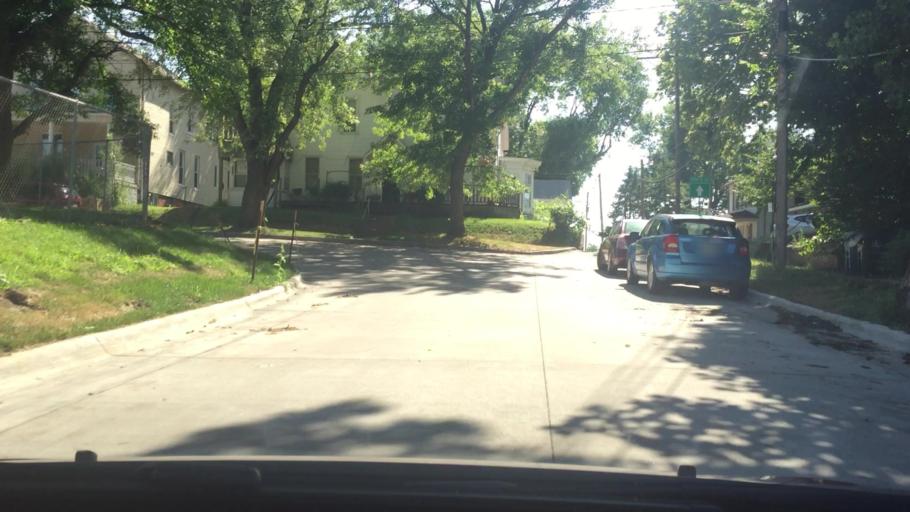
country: US
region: Iowa
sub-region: Muscatine County
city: Muscatine
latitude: 41.4195
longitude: -91.0542
